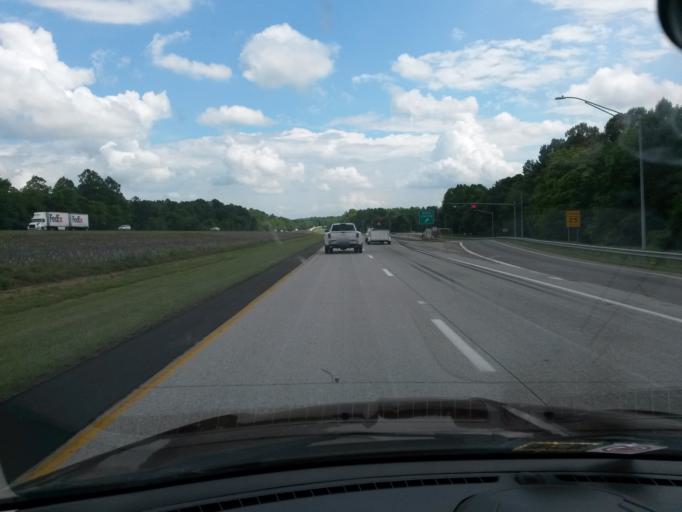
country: US
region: Virginia
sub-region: Carroll County
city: Cana
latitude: 36.5278
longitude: -80.7486
